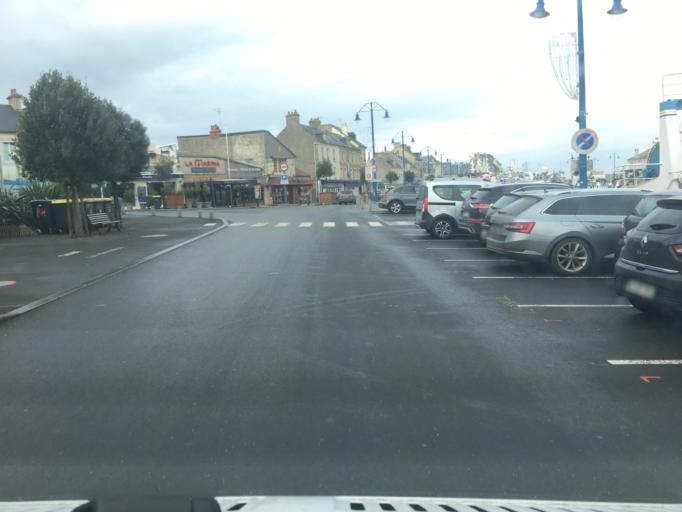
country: FR
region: Lower Normandy
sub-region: Departement du Calvados
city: Port-en-Bessin-Huppain
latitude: 49.3469
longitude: -0.7544
